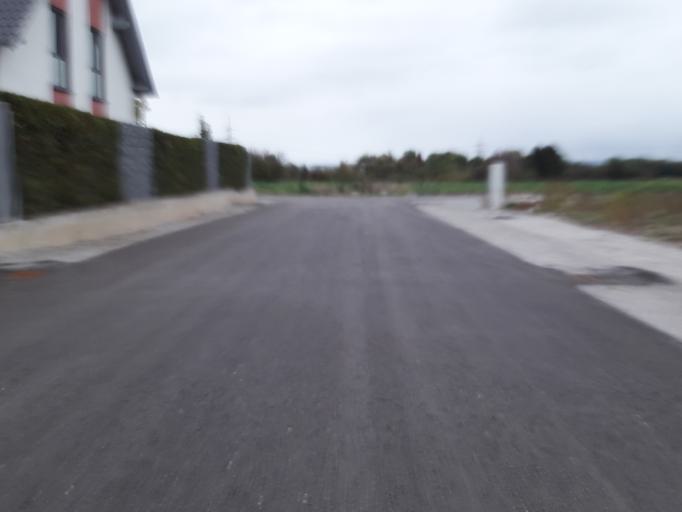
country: DE
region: North Rhine-Westphalia
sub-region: Regierungsbezirk Detmold
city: Paderborn
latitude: 51.6954
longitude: 8.7138
